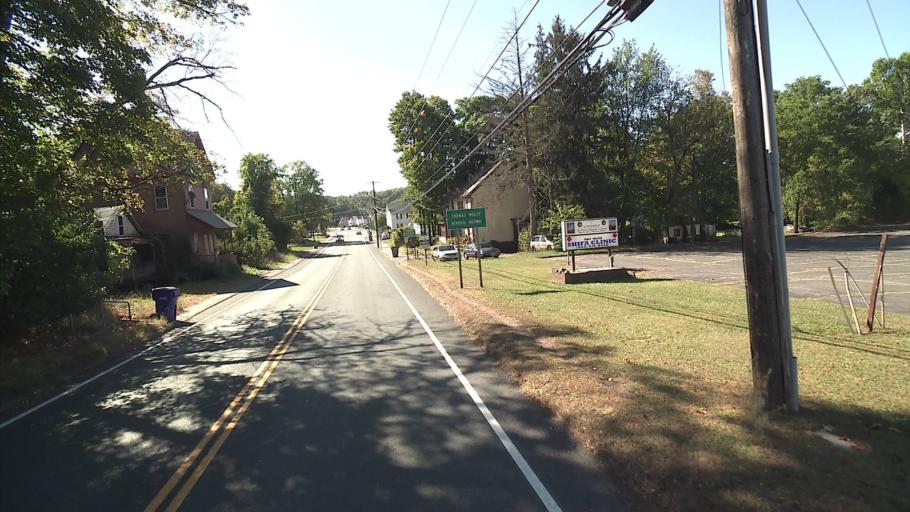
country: US
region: Connecticut
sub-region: Tolland County
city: Rockville
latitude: 41.8705
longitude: -72.4643
